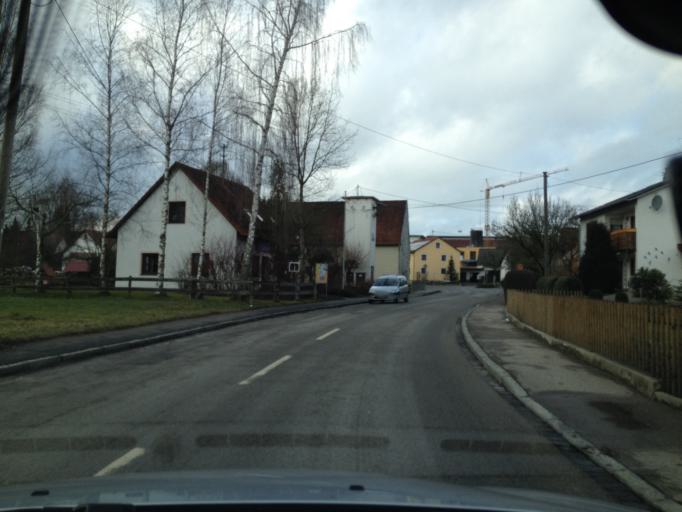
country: DE
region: Bavaria
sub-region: Swabia
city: Fischach
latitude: 48.2499
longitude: 10.6971
